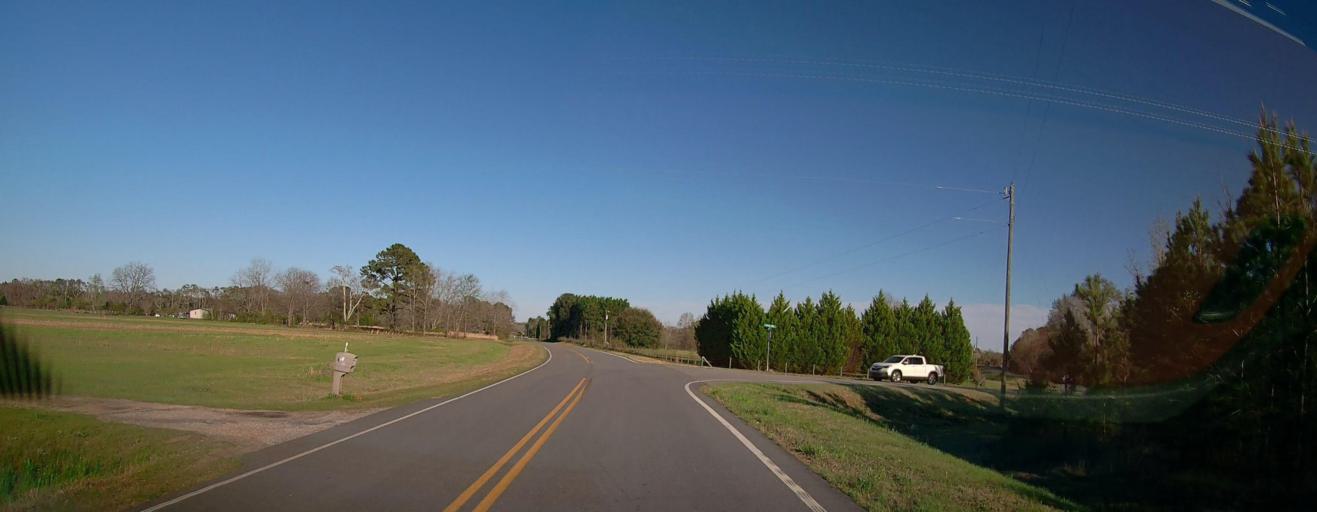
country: US
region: Georgia
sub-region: Dooly County
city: Unadilla
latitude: 32.3481
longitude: -83.6153
